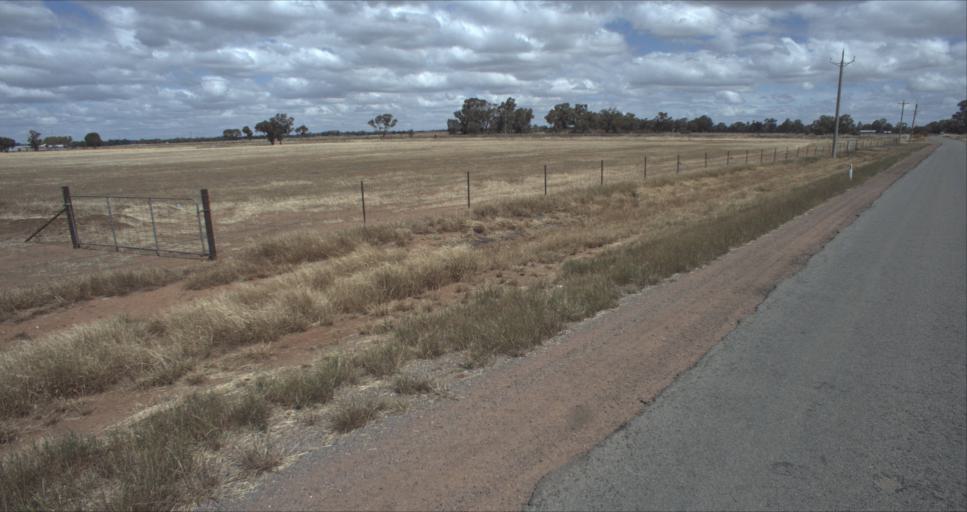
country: AU
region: New South Wales
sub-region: Leeton
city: Leeton
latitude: -34.5884
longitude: 146.3707
